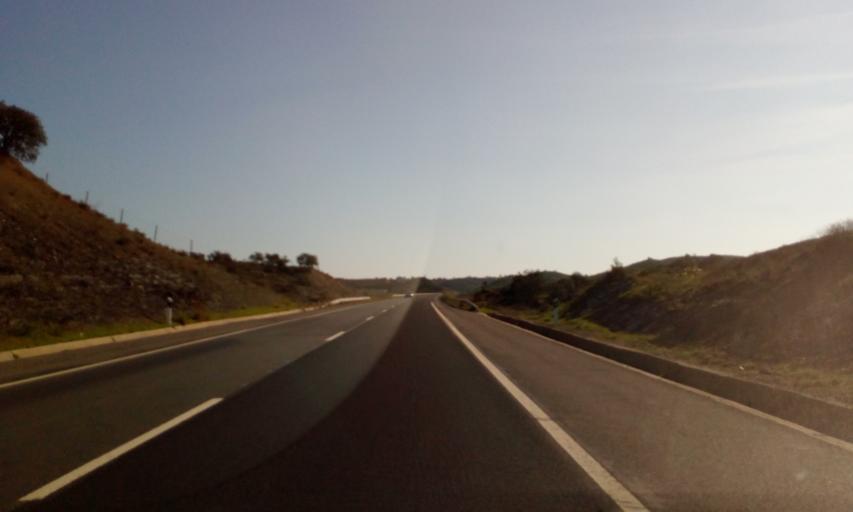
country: PT
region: Faro
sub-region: Castro Marim
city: Castro Marim
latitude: 37.2521
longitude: -7.4767
